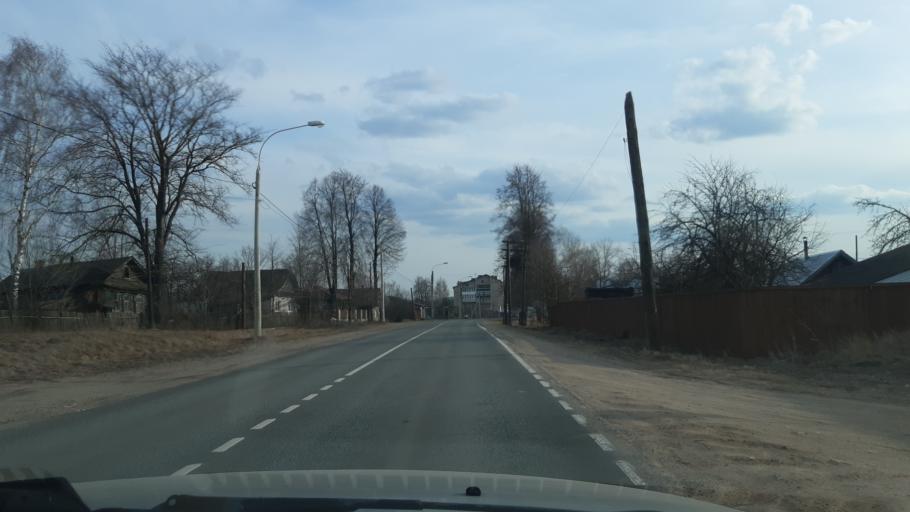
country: RU
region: Vladimir
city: Nikologory
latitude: 56.1513
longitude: 41.9957
